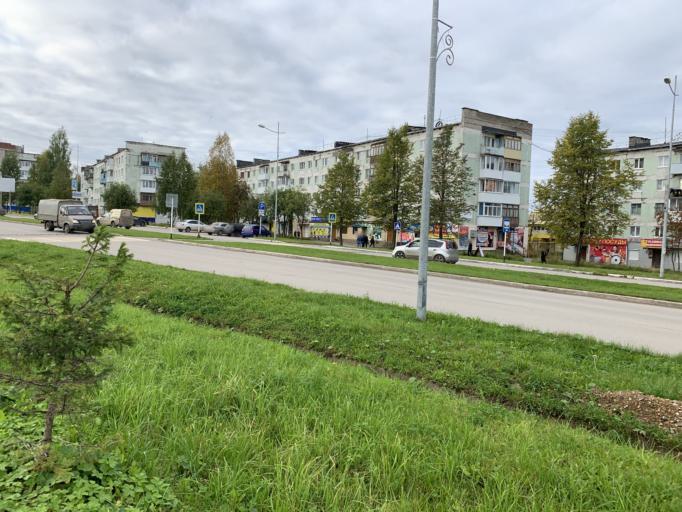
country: RU
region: Perm
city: Gubakha
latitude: 58.8344
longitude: 57.5568
